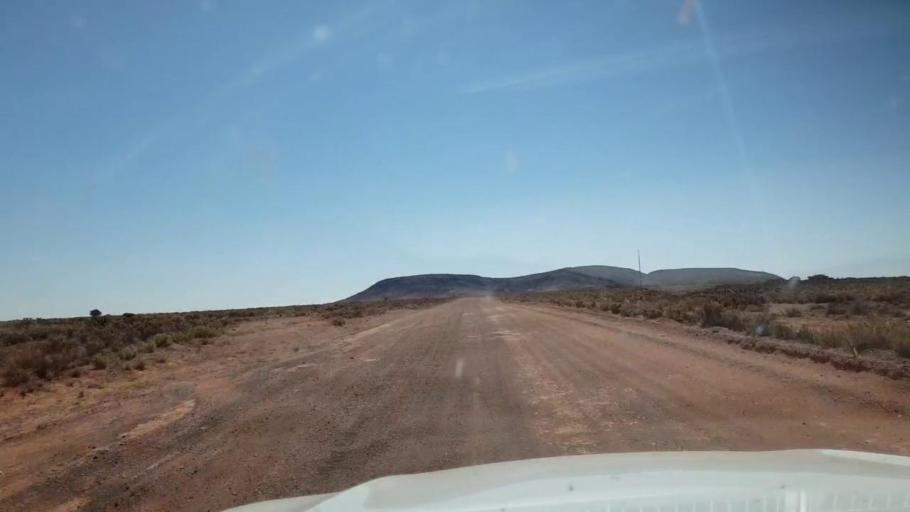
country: AU
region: South Australia
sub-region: Whyalla
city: Whyalla
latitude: -32.7076
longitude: 137.1384
